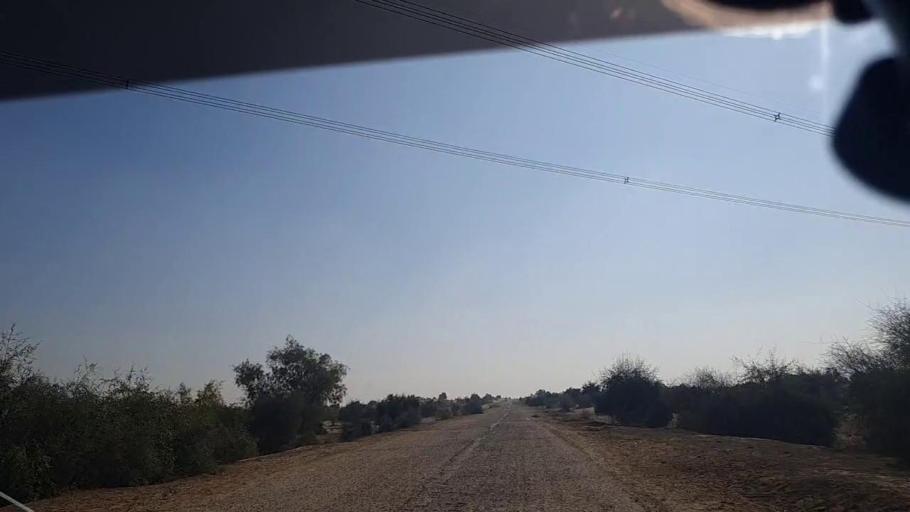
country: PK
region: Sindh
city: Khanpur
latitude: 27.5786
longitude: 69.3054
